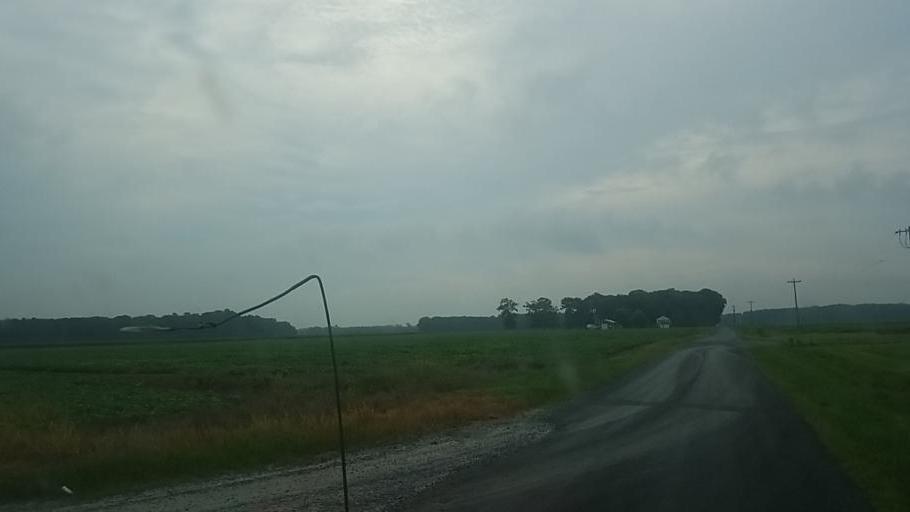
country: US
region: Delaware
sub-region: Sussex County
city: Selbyville
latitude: 38.4432
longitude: -75.2673
